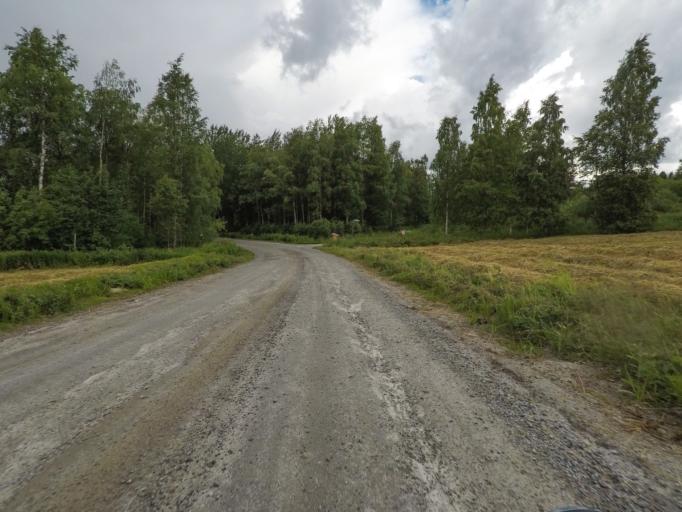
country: FI
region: Central Finland
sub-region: Jyvaeskylae
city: Hankasalmi
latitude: 62.4171
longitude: 26.6231
